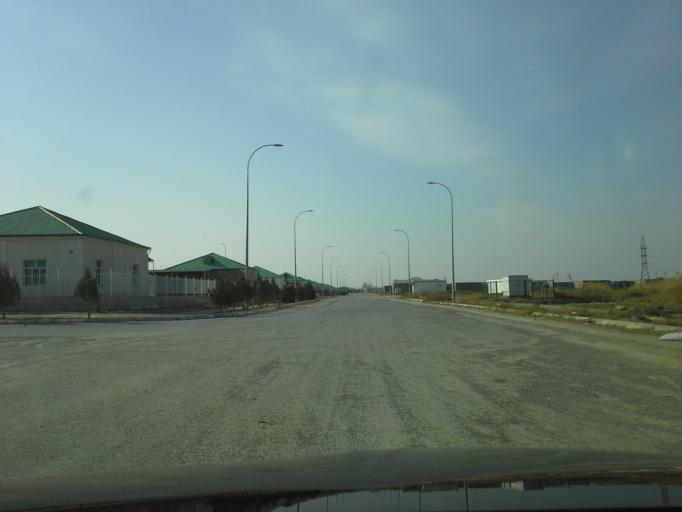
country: TM
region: Ahal
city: Abadan
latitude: 38.1738
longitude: 58.0544
